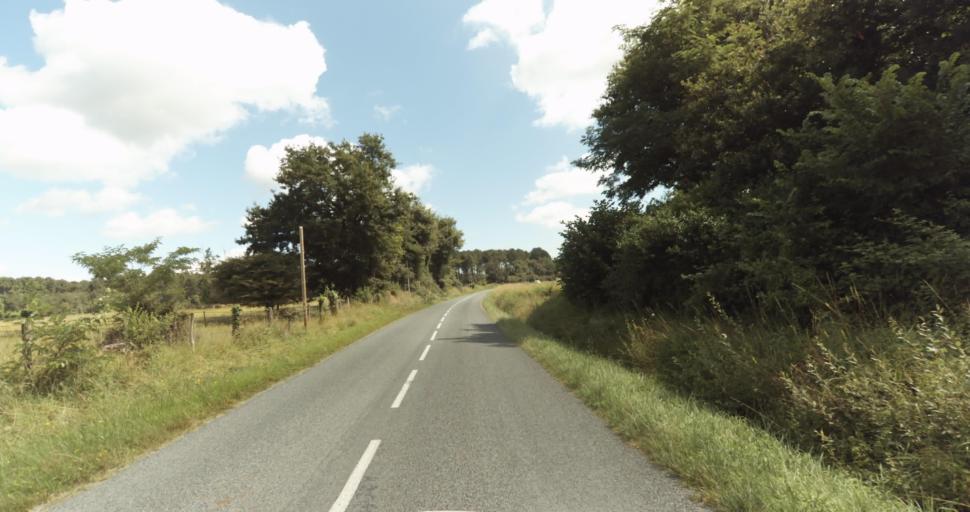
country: FR
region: Aquitaine
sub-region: Departement de la Gironde
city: Bazas
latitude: 44.4554
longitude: -0.1970
